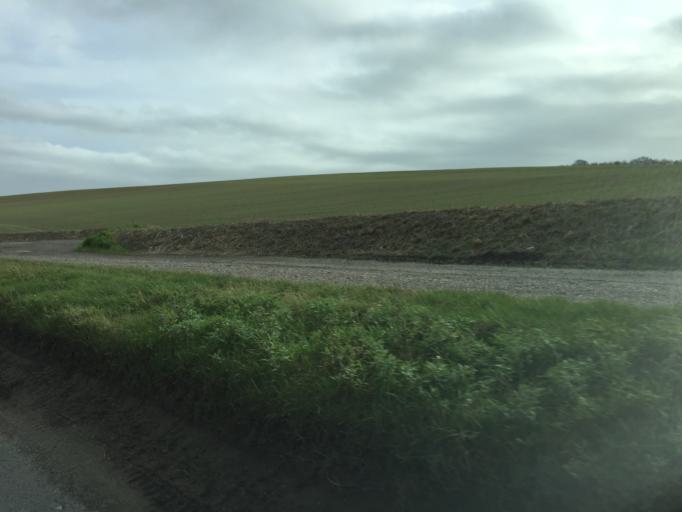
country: GB
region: England
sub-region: Oxfordshire
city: Blewbury
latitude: 51.5664
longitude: -1.2197
